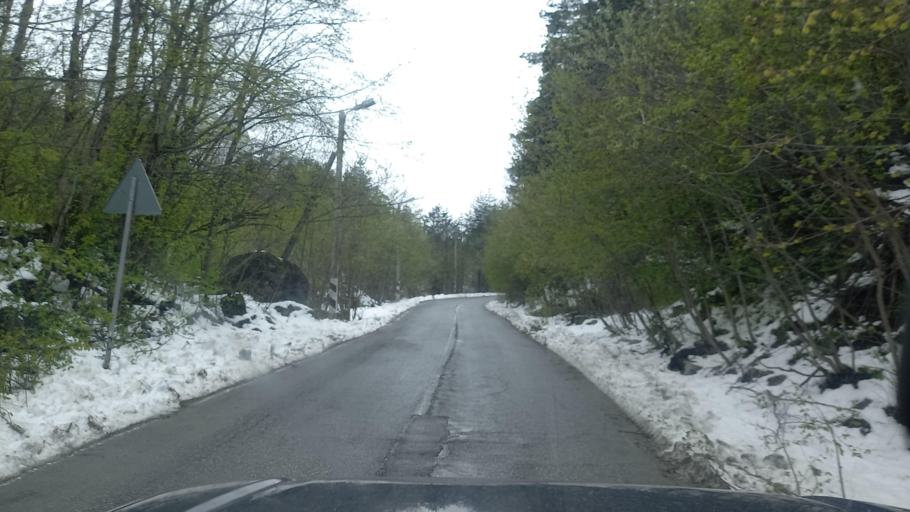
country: RU
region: North Ossetia
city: Mizur
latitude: 42.7913
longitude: 43.9140
